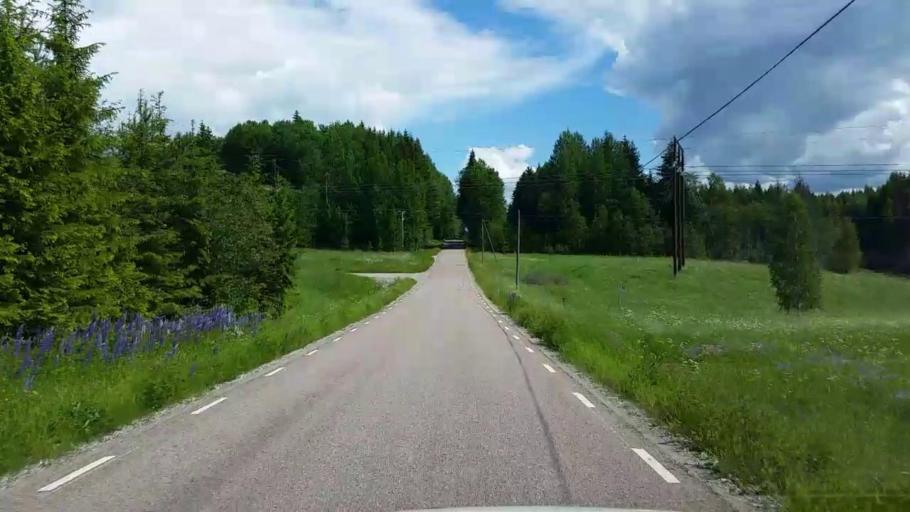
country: SE
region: Vaestmanland
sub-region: Fagersta Kommun
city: Fagersta
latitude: 60.0017
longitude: 15.7595
